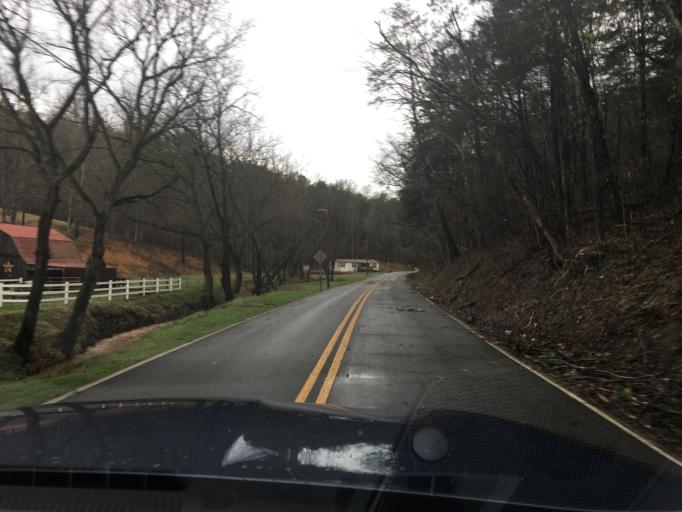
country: US
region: Tennessee
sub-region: McMinn County
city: Englewood
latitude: 35.3645
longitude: -84.4369
